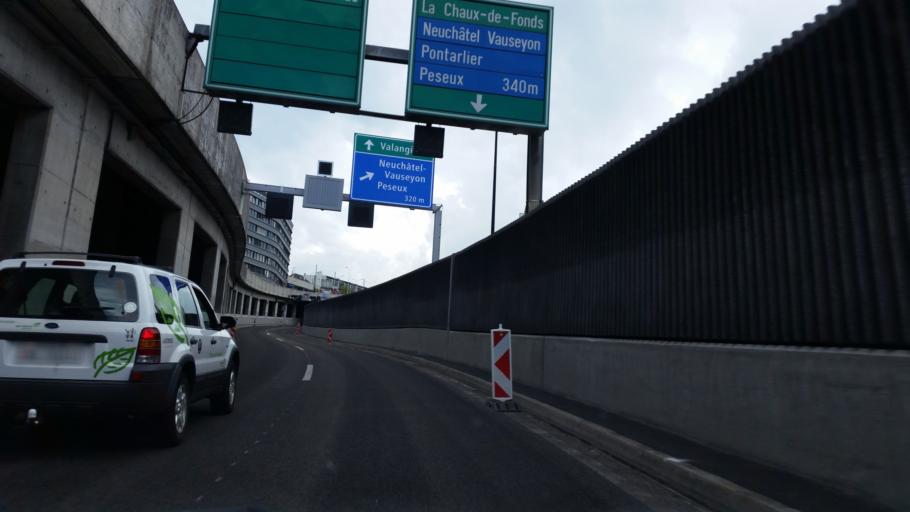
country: CH
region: Neuchatel
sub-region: Neuchatel District
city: Neuchatel
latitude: 46.9898
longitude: 6.9146
